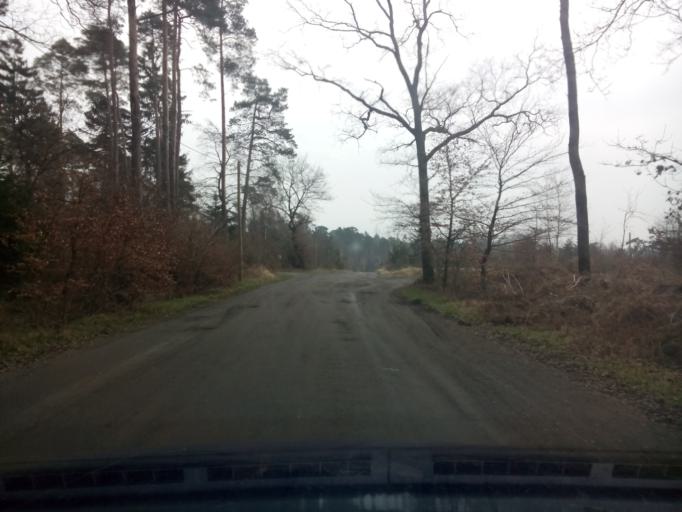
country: DE
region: Lower Saxony
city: Drangstedt
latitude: 53.6131
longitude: 8.7282
